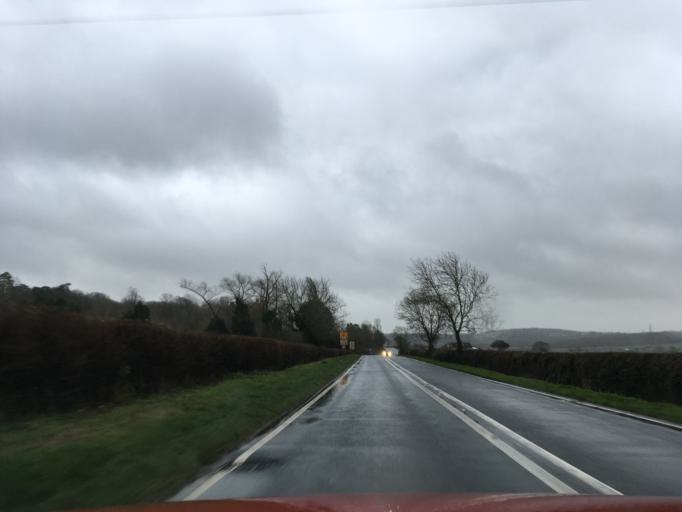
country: GB
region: England
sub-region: Oxfordshire
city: Eynsham
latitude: 51.7580
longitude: -1.3400
